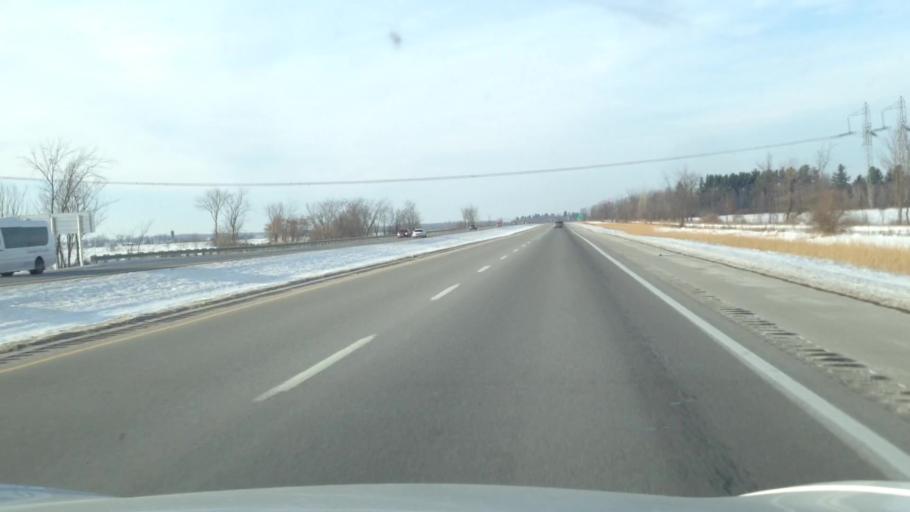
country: CA
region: Quebec
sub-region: Monteregie
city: Rigaud
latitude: 45.5042
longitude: -74.3635
